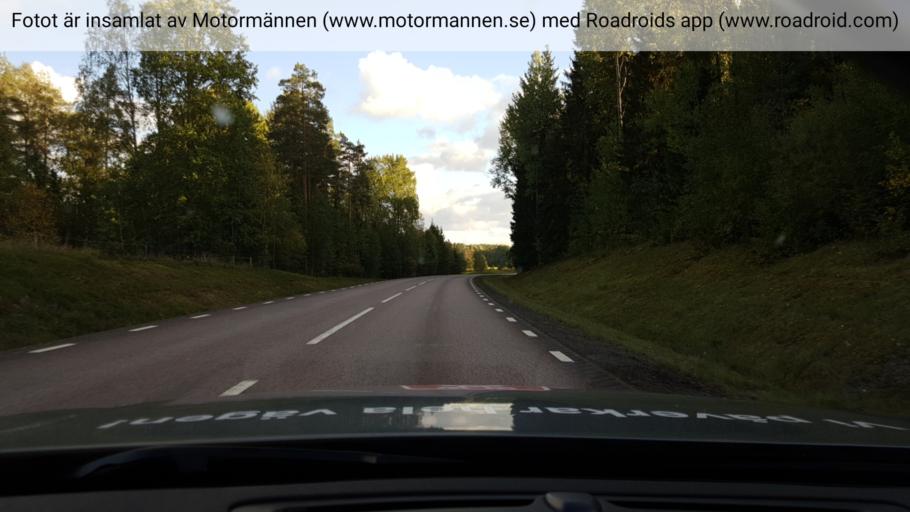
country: SE
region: Vaermland
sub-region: Karlstads Kommun
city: Molkom
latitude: 59.6271
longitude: 13.7294
